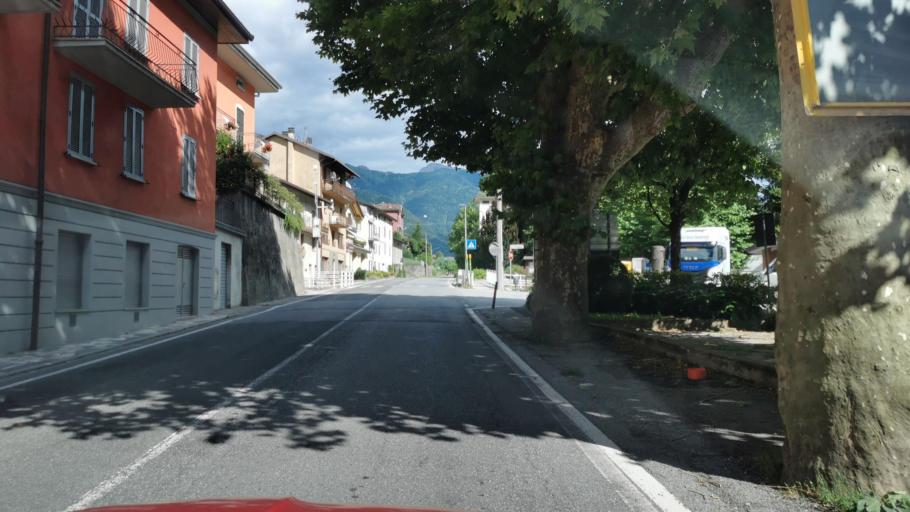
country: IT
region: Lombardy
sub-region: Provincia di Lecco
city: Primaluna
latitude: 45.9896
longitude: 9.4156
